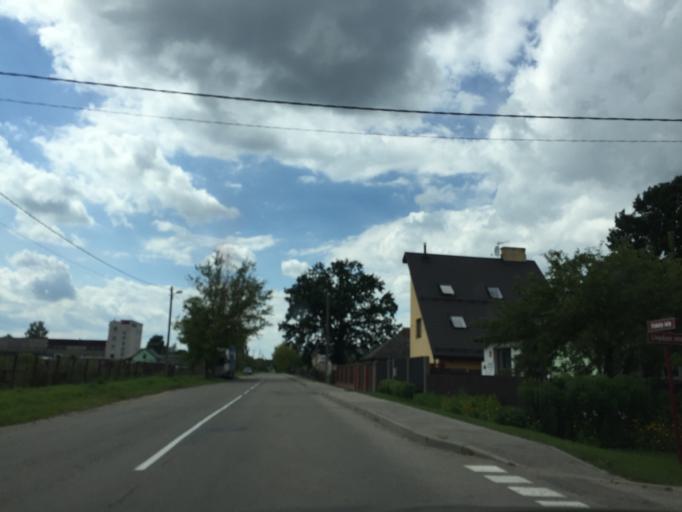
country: LV
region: Jelgava
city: Jelgava
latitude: 56.6254
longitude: 23.7095
